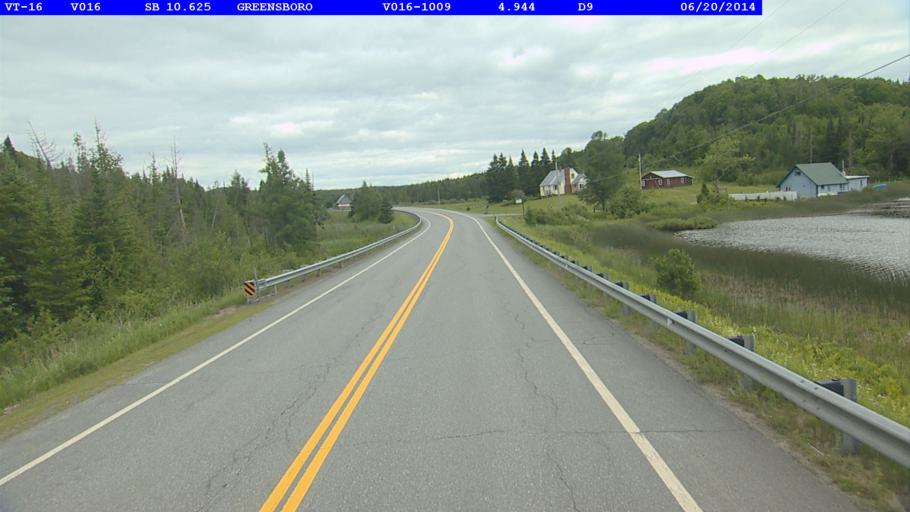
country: US
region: Vermont
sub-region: Caledonia County
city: Hardwick
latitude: 44.6163
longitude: -72.2087
